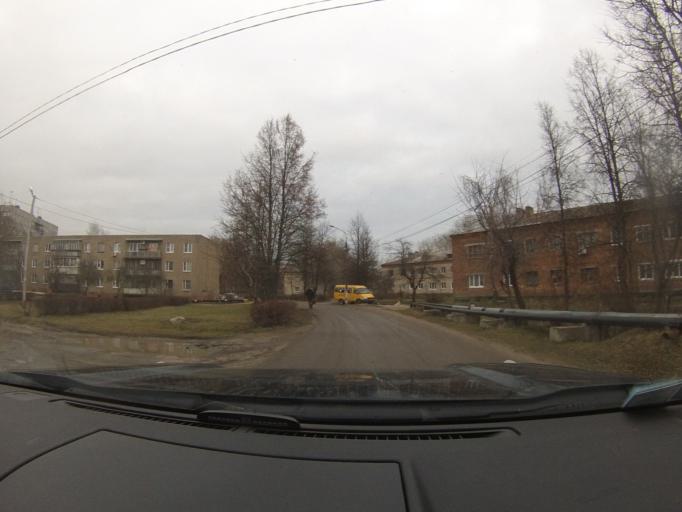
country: RU
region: Moskovskaya
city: Lopatinskiy
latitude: 55.3218
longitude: 38.7040
